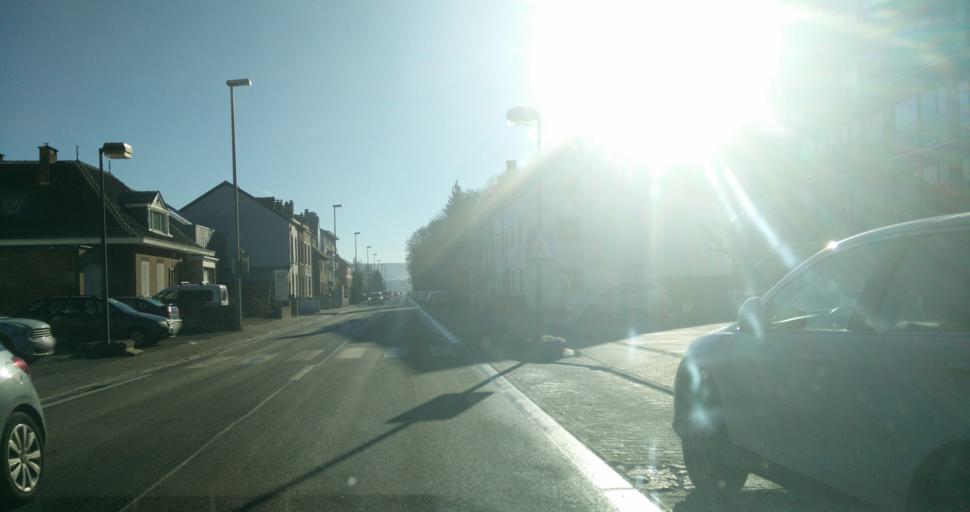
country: BE
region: Wallonia
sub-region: Province de Namur
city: Namur
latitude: 50.4398
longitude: 4.8591
